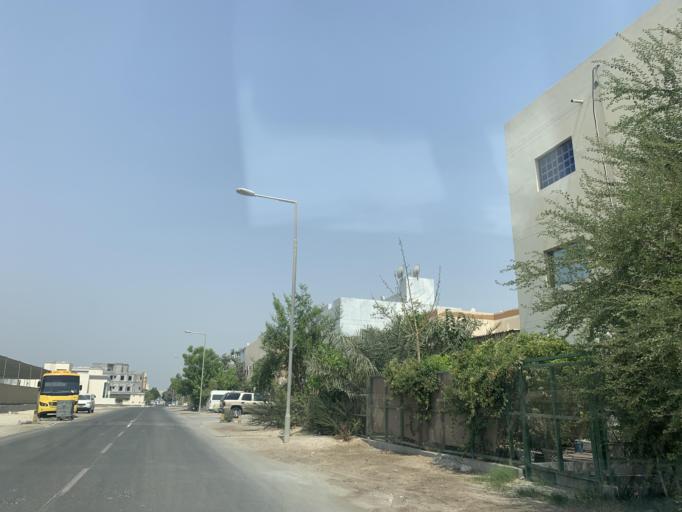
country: BH
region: Manama
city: Jidd Hafs
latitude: 26.2075
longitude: 50.5081
